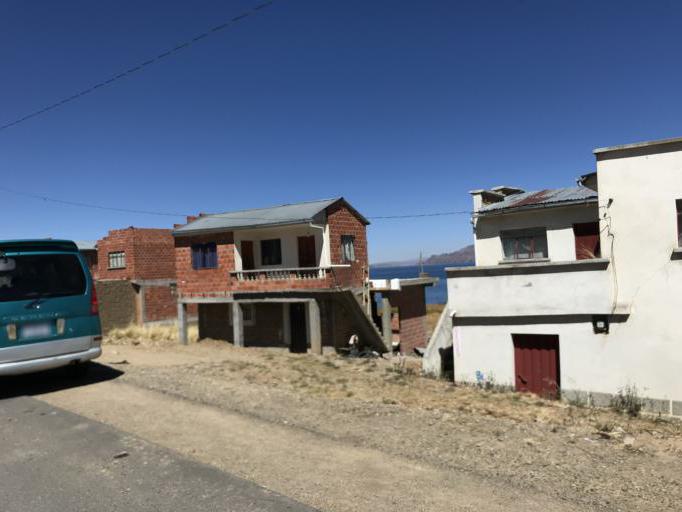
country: BO
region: La Paz
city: Huatajata
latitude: -16.2155
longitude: -68.6687
